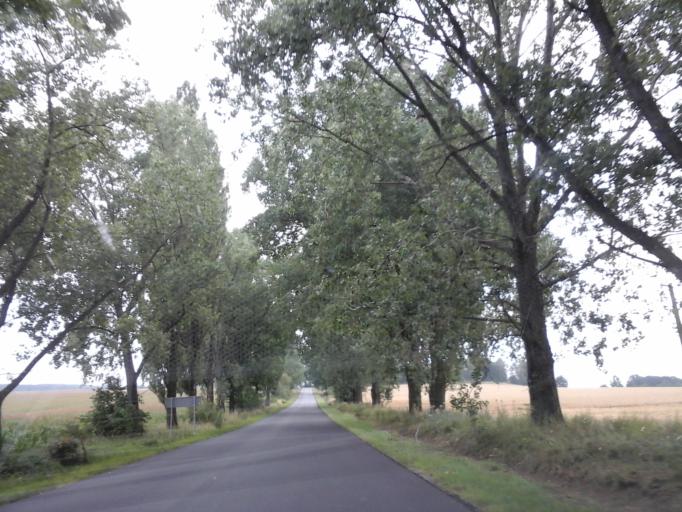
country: PL
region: Lower Silesian Voivodeship
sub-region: Powiat zabkowicki
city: Cieplowody
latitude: 50.6440
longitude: 16.8907
